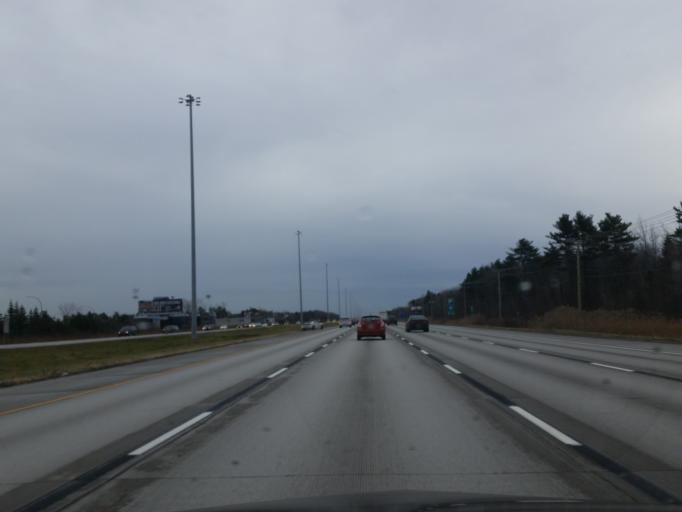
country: CA
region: Quebec
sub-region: Laurentides
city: Blainville
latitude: 45.6651
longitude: -73.8967
